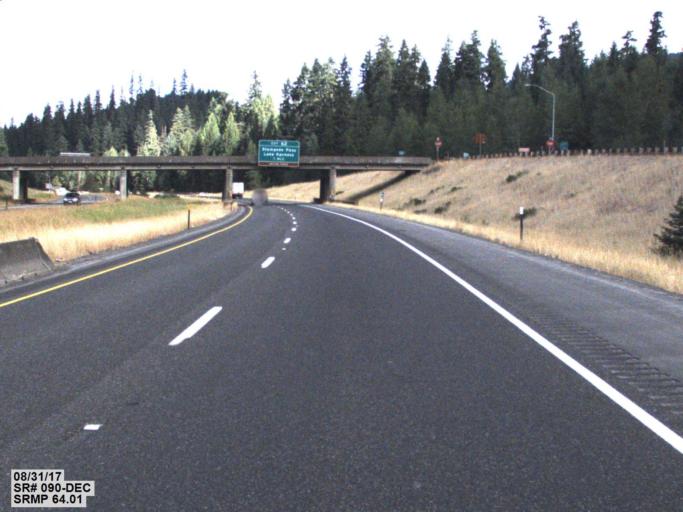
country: US
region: Washington
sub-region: Kittitas County
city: Cle Elum
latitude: 47.2970
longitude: -121.2875
